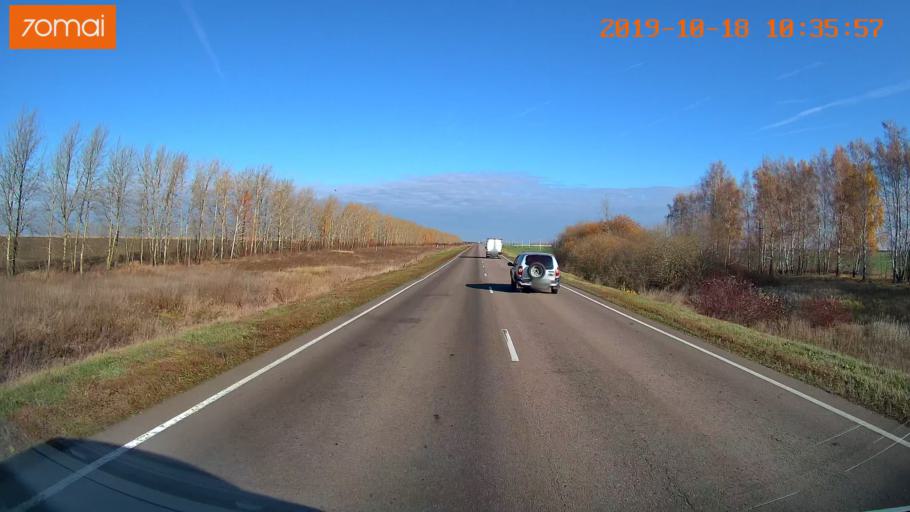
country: RU
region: Tula
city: Kurkino
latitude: 53.5408
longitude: 38.6228
